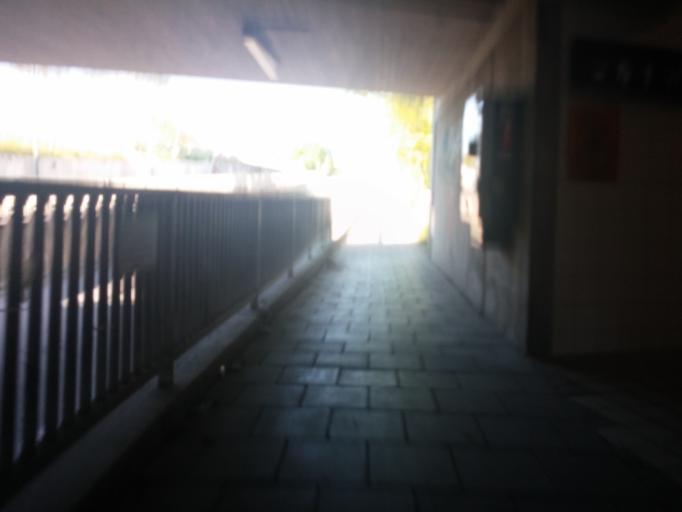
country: DE
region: Bavaria
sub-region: Upper Bavaria
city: Haar
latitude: 48.1183
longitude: 11.6988
